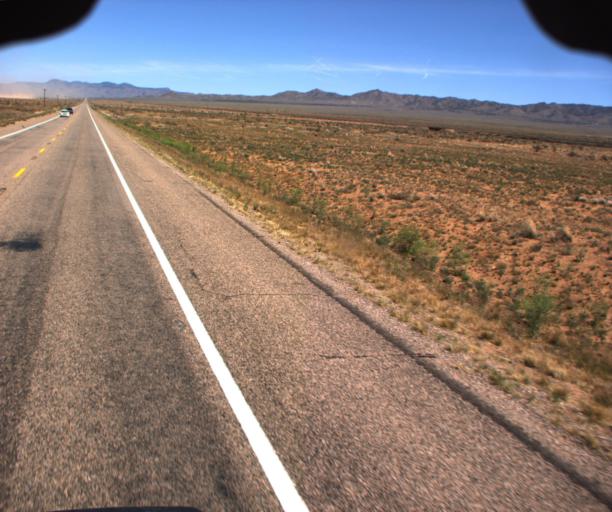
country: US
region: Arizona
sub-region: Mohave County
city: New Kingman-Butler
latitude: 35.3239
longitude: -113.9087
